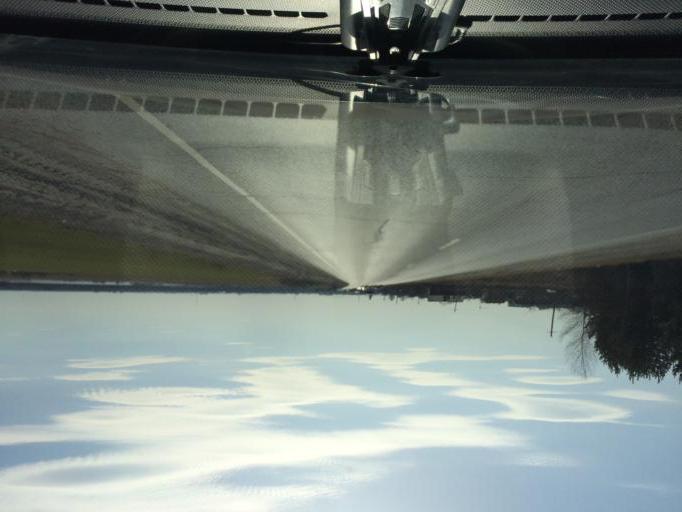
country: RU
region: Mariy-El
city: Yoshkar-Ola
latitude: 56.6658
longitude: 47.9902
